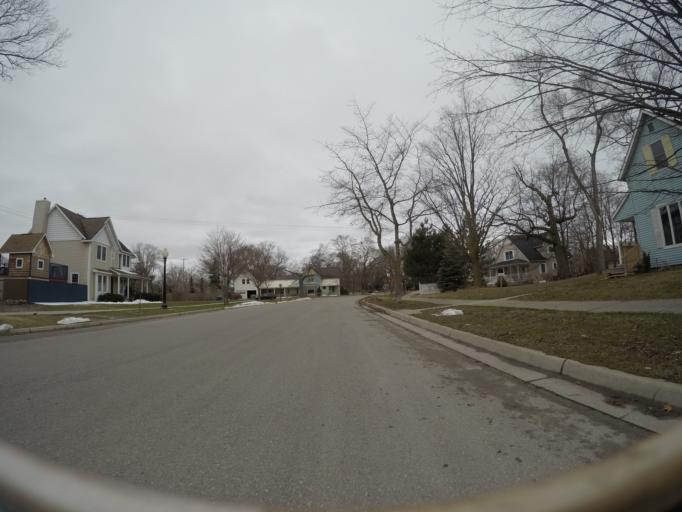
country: US
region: Michigan
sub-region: Grand Traverse County
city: Traverse City
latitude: 44.7605
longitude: -85.6079
